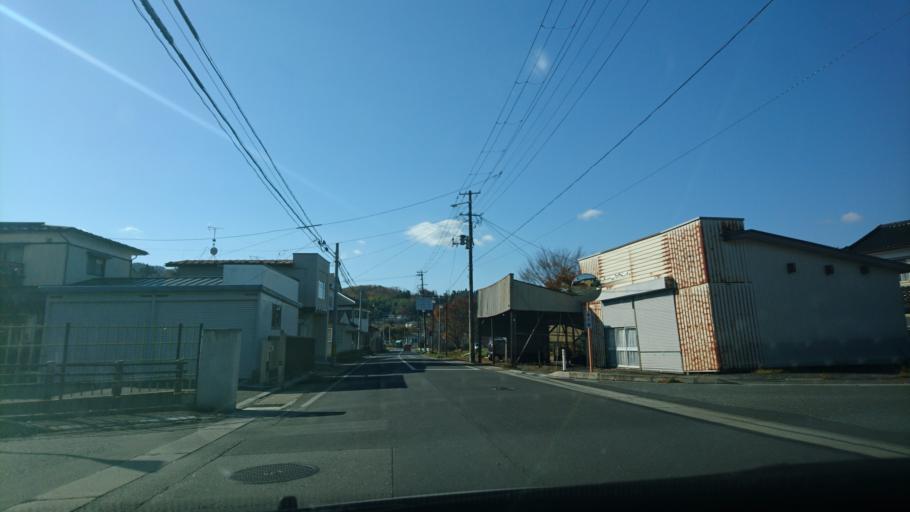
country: JP
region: Iwate
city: Ichinoseki
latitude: 39.0141
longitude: 141.3954
